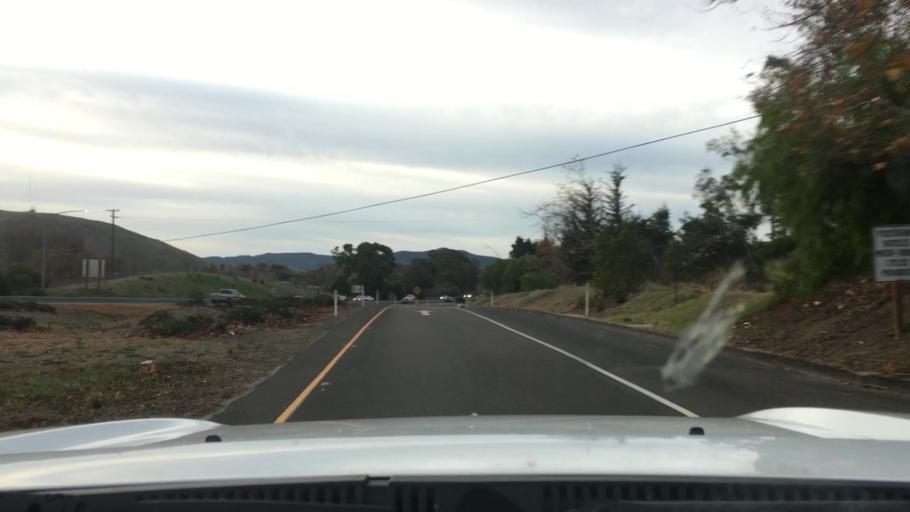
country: US
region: California
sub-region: San Luis Obispo County
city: San Luis Obispo
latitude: 35.2737
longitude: -120.6723
